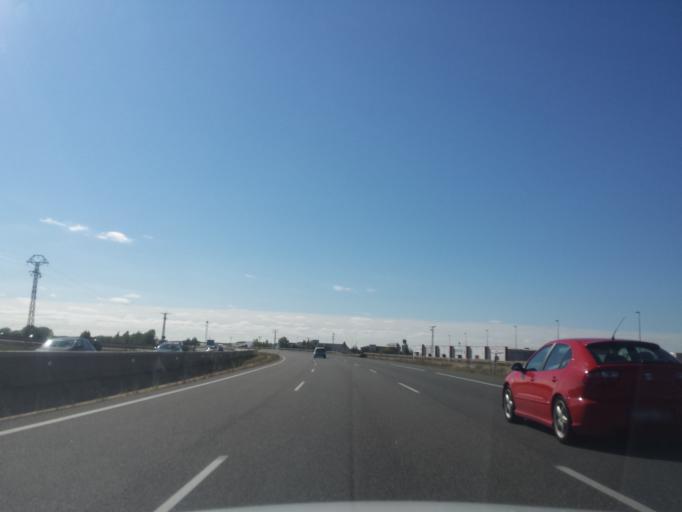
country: ES
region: Castille and Leon
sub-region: Provincia de Zamora
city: Benavente
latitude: 41.9995
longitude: -5.6563
